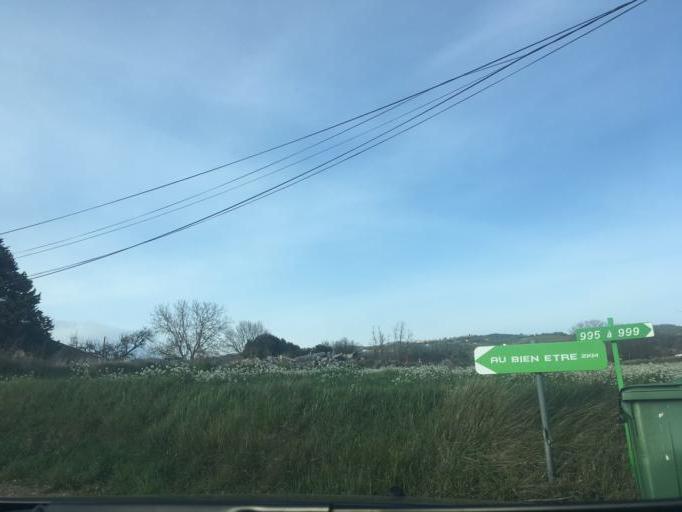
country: FR
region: Provence-Alpes-Cote d'Azur
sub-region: Departement du Var
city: Villecroze
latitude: 43.5611
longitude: 6.2818
